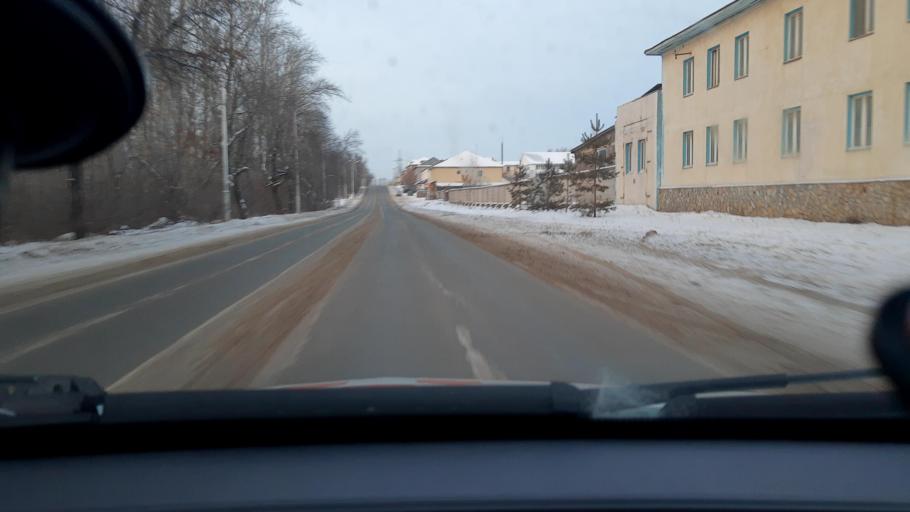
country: RU
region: Bashkortostan
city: Blagoveshchensk
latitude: 54.8973
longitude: 56.0543
